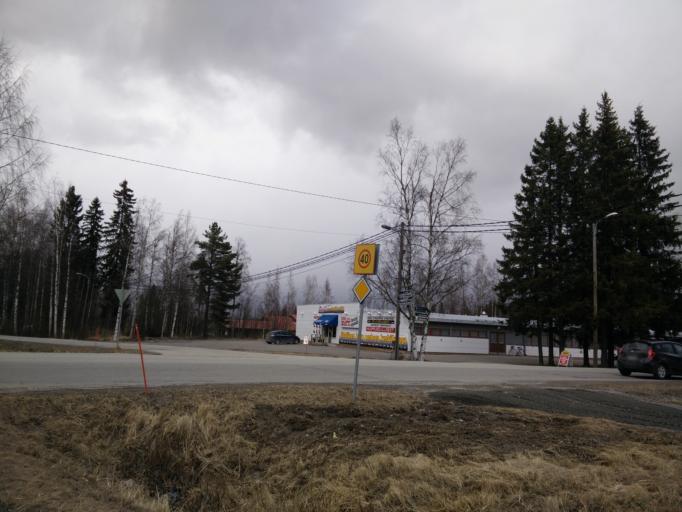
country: FI
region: Pirkanmaa
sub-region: Tampere
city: Orivesi
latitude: 61.6927
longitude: 24.3547
